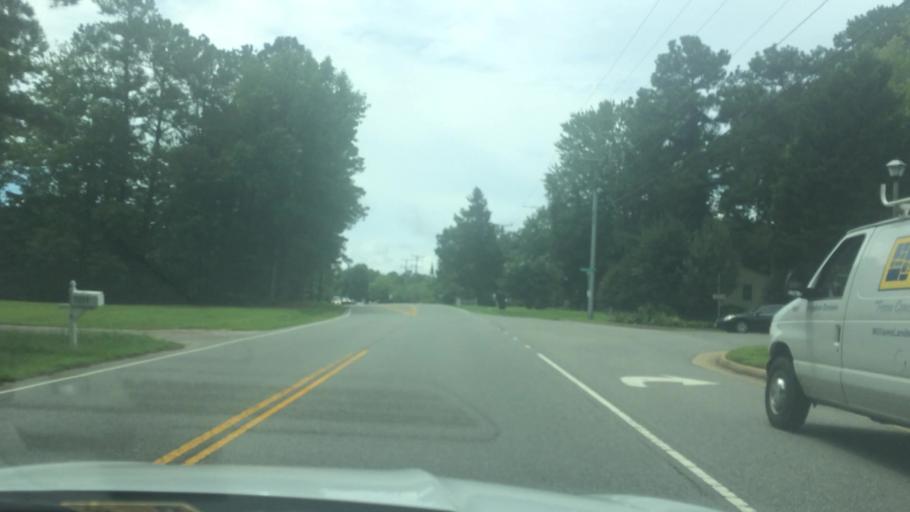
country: US
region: Virginia
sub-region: James City County
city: Williamsburg
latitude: 37.2560
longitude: -76.7657
